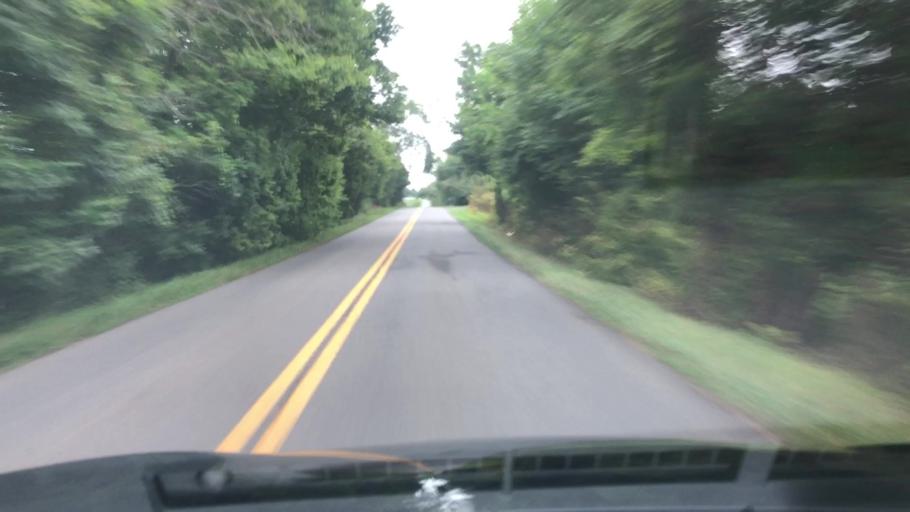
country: US
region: Virginia
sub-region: Prince William County
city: Nokesville
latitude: 38.6724
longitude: -77.6534
